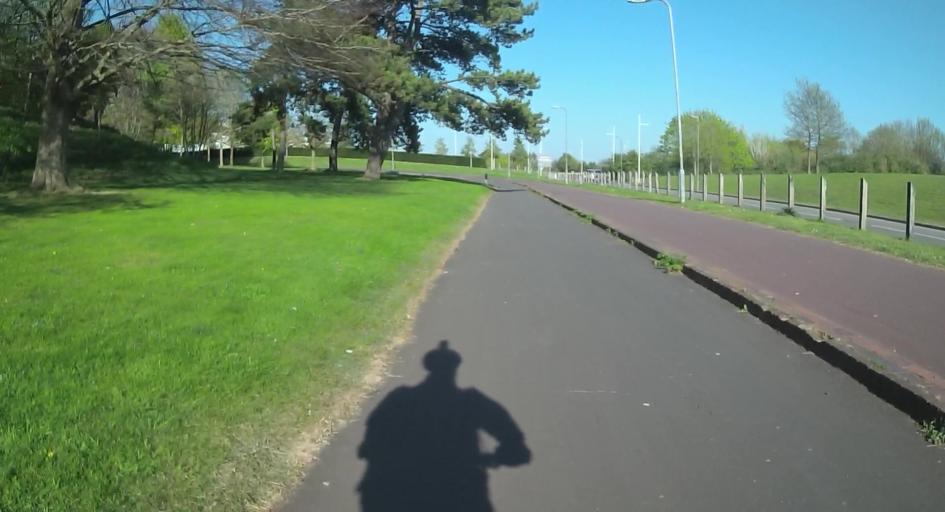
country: GB
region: England
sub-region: Hampshire
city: Basingstoke
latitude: 51.2657
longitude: -1.1137
